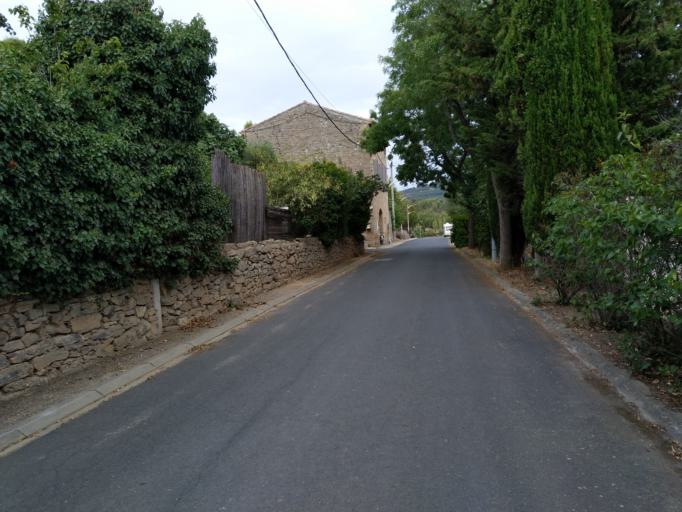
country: FR
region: Languedoc-Roussillon
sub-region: Departement de l'Herault
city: Olonzac
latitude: 43.2981
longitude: 2.7599
